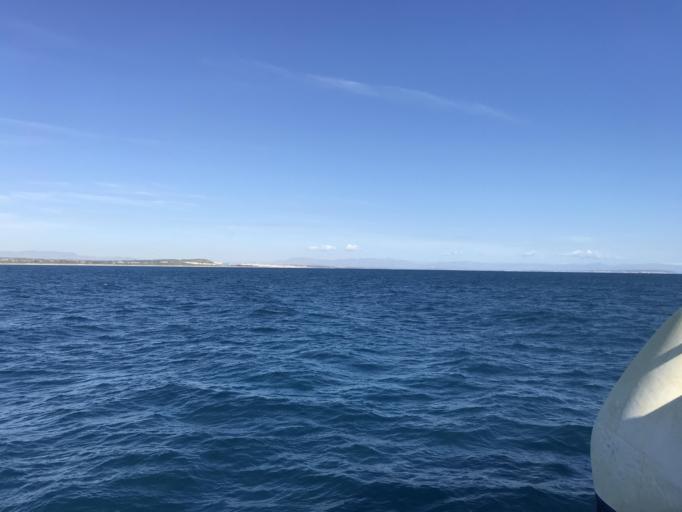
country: ES
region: Valencia
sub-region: Provincia de Alicante
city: Torrevieja
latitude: 38.0096
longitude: -0.6302
